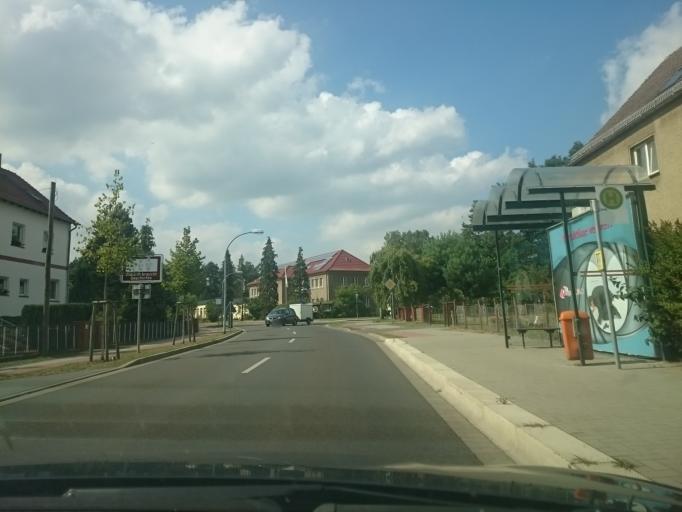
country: DE
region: Mecklenburg-Vorpommern
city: Torgelow
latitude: 53.6318
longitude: 13.9958
